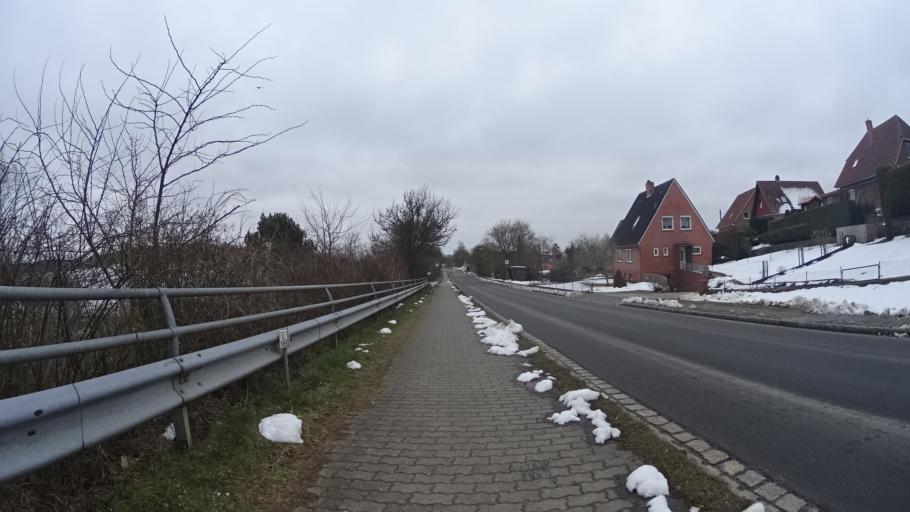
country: DE
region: Schleswig-Holstein
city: Panker
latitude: 54.3103
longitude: 10.5736
